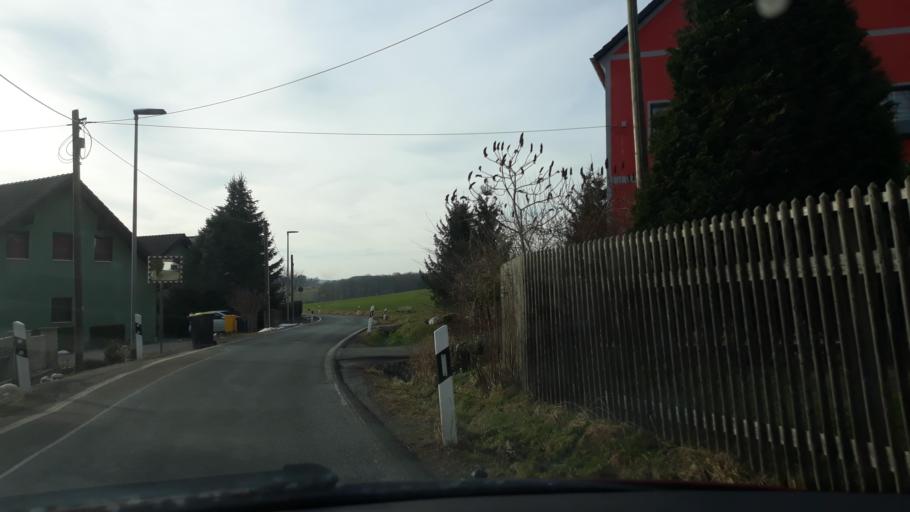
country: DE
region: Saxony
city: Wilkau-Hasslau
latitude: 50.6507
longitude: 12.5064
